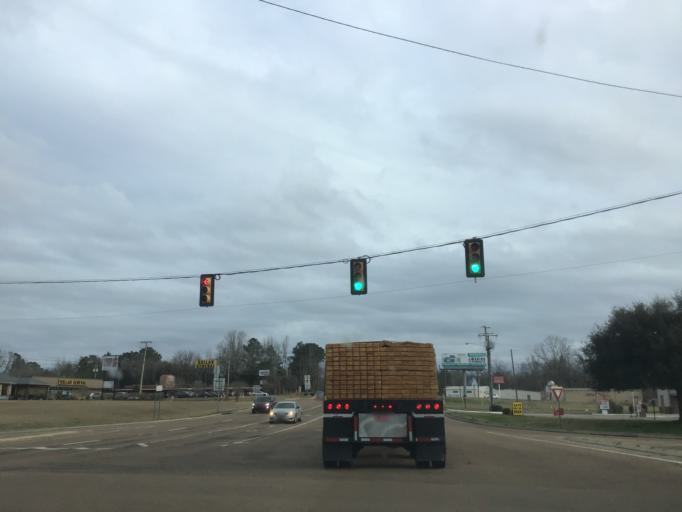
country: US
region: Mississippi
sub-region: Warren County
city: Beechwood
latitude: 32.3444
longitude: -90.8292
